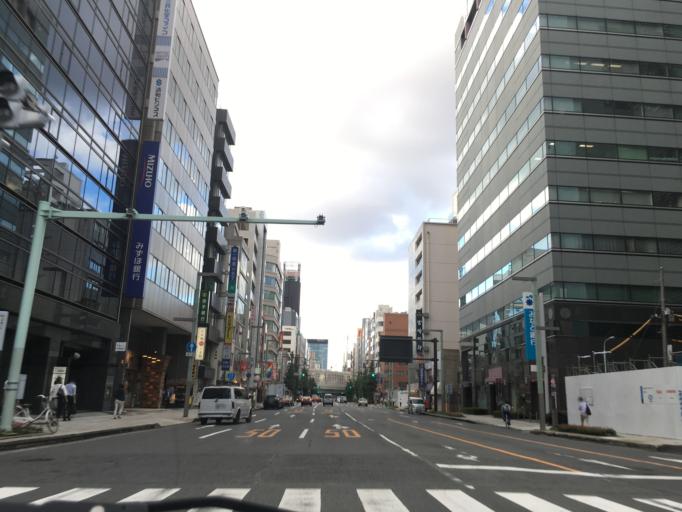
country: JP
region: Tokyo
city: Tokyo
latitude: 35.6887
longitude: 139.7730
